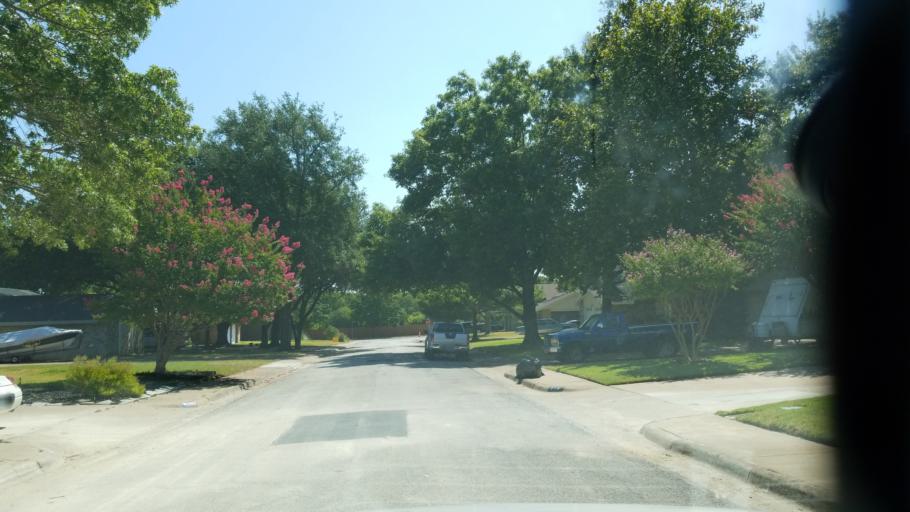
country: US
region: Texas
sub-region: Dallas County
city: Duncanville
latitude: 32.6469
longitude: -96.8974
